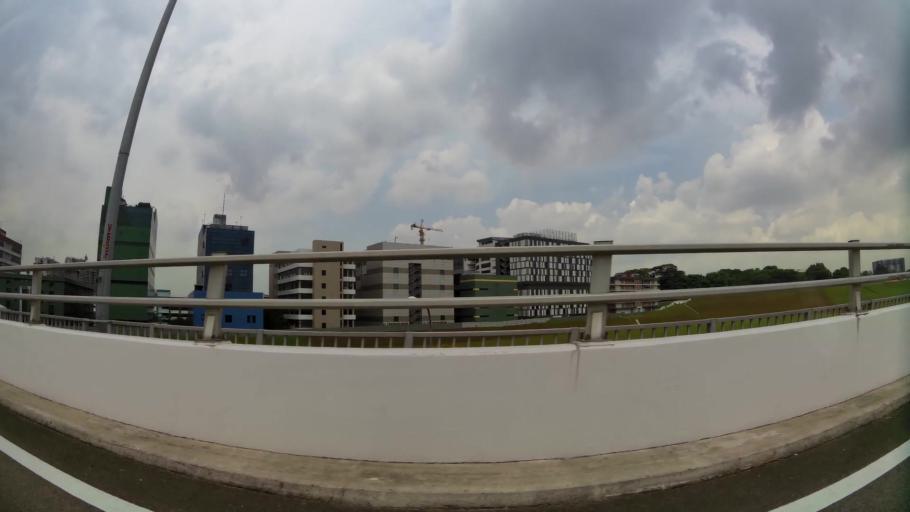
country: SG
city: Singapore
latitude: 1.3415
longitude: 103.8872
